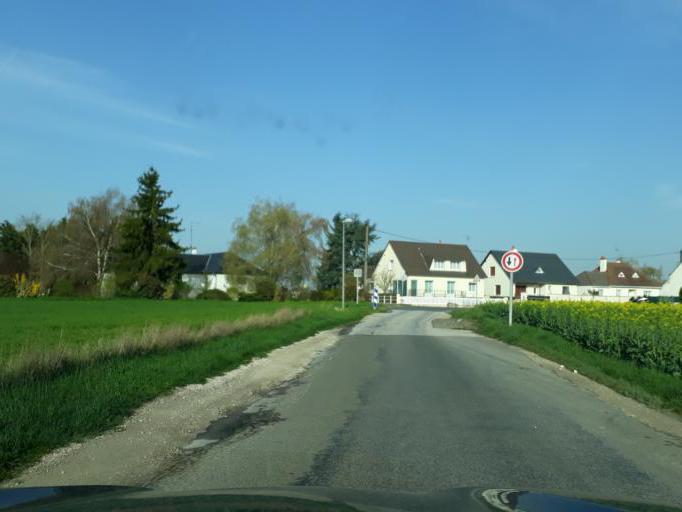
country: FR
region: Centre
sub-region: Departement du Loiret
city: Ingre
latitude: 47.9129
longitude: 1.8176
